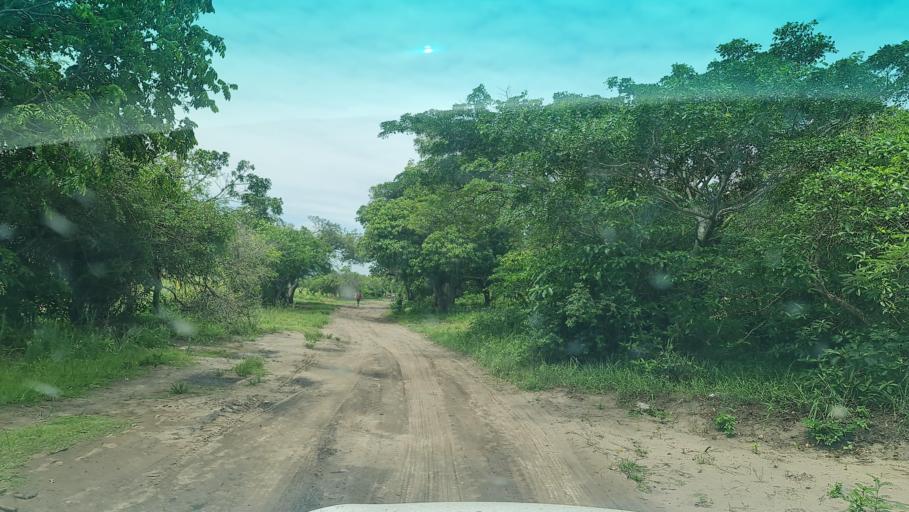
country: MZ
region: Maputo
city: Manhica
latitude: -25.5198
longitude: 32.8645
